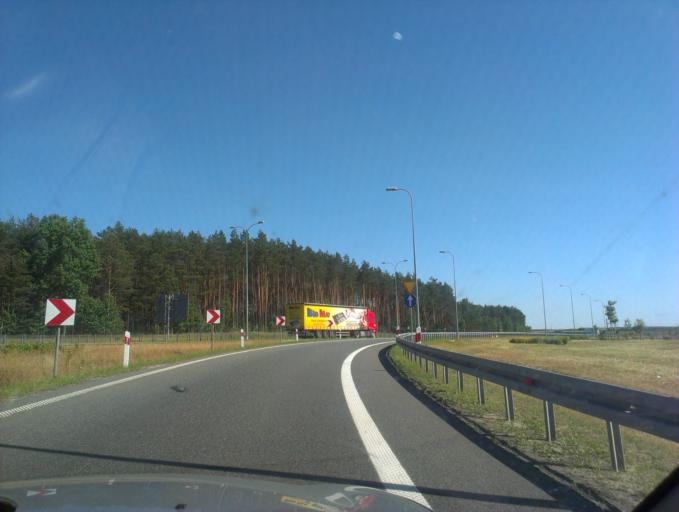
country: PL
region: Kujawsko-Pomorskie
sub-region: Powiat swiecki
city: Warlubie
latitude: 53.4717
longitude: 18.6172
